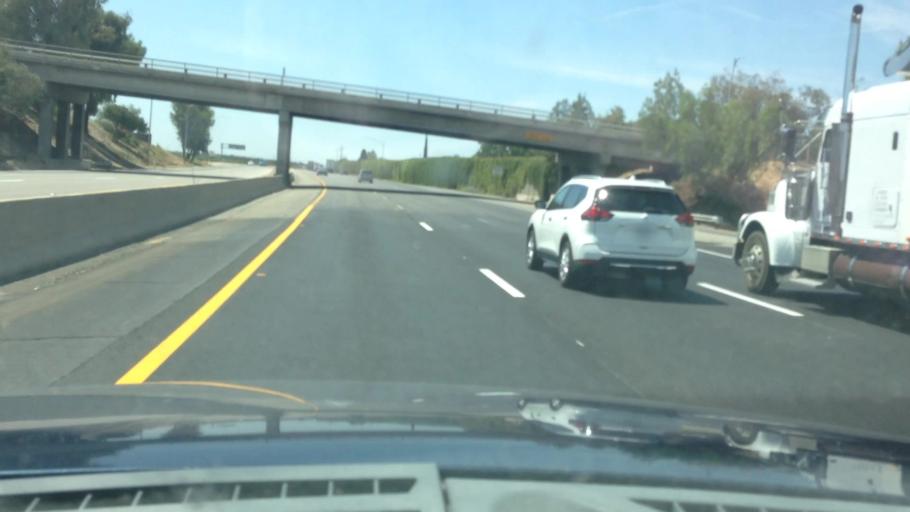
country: US
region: California
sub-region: Kern County
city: McFarland
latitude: 35.6739
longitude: -119.2266
